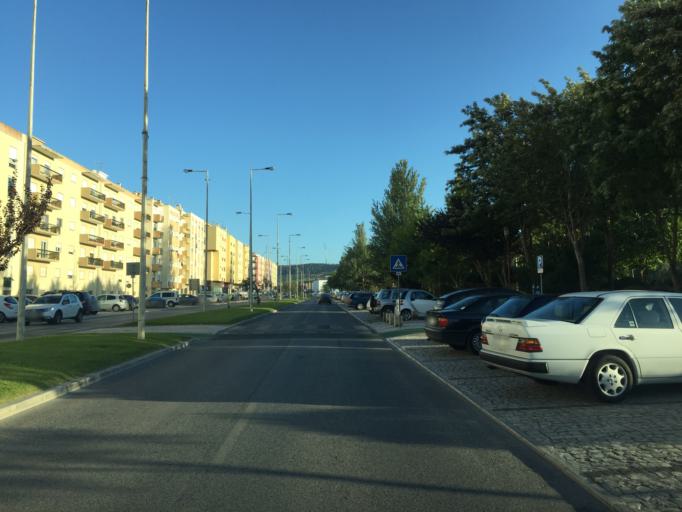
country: PT
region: Lisbon
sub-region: Torres Vedras
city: Torres Vedras
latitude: 39.0878
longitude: -9.2612
